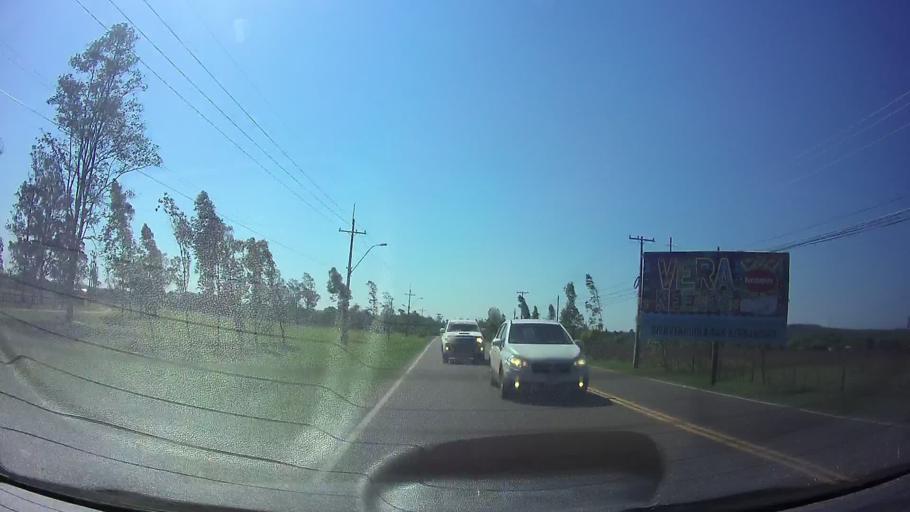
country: PY
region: Cordillera
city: San Bernardino
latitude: -25.3507
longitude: -57.2694
